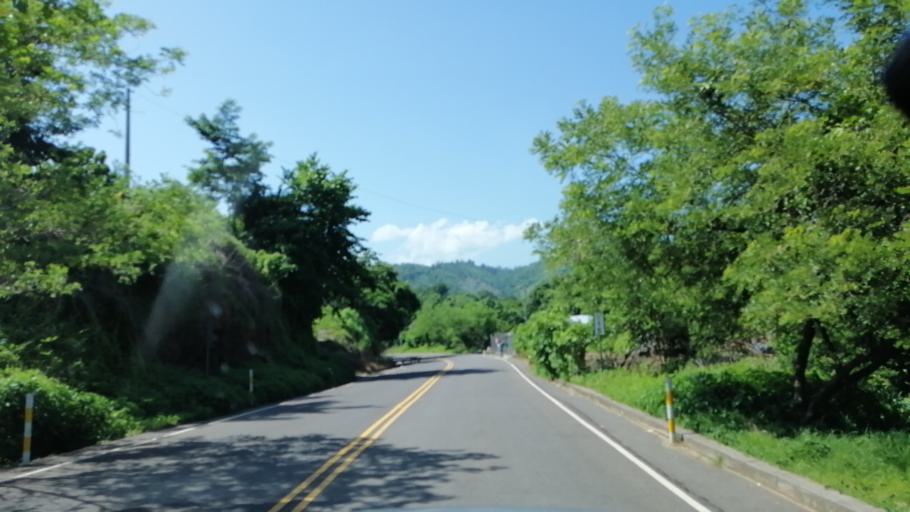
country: HN
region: Lempira
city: La Virtud
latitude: 13.9545
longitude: -88.7438
